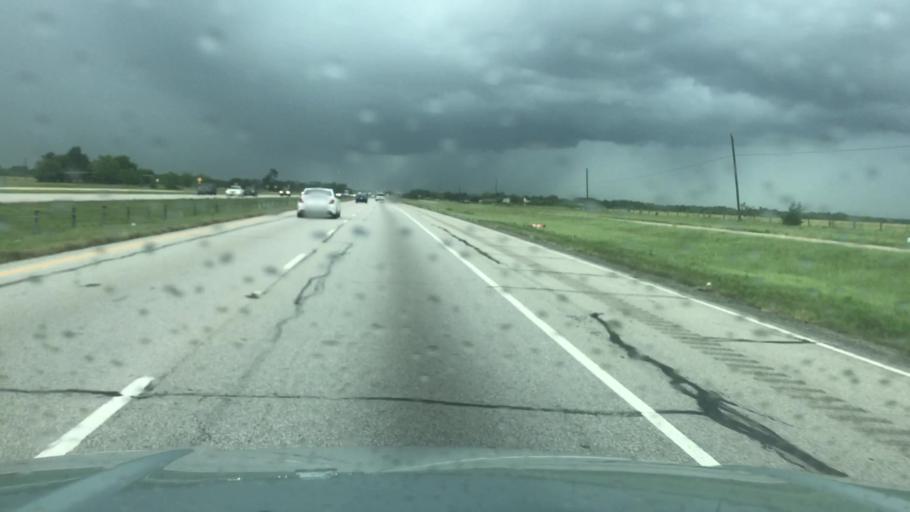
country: US
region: Texas
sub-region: Austin County
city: Sealy
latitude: 29.7504
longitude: -96.2868
